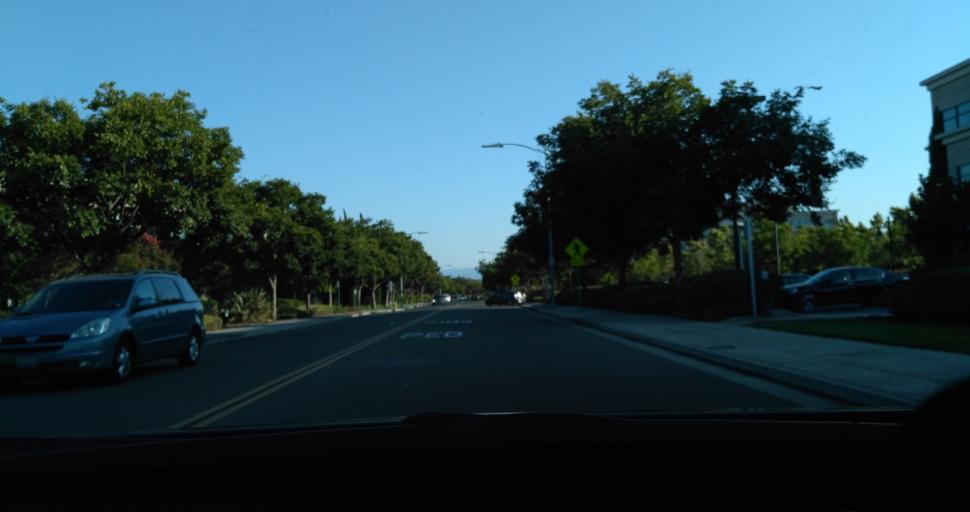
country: US
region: California
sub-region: Santa Clara County
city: Milpitas
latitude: 37.4095
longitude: -121.9282
